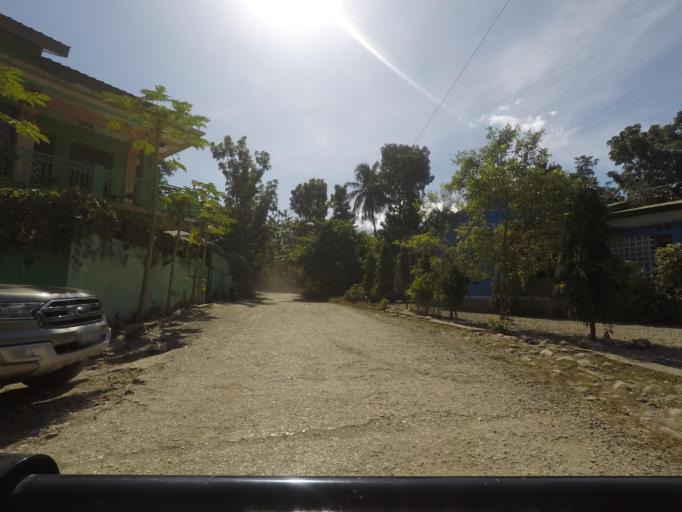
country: TL
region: Bobonaro
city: Maliana
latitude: -8.9928
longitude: 125.2194
